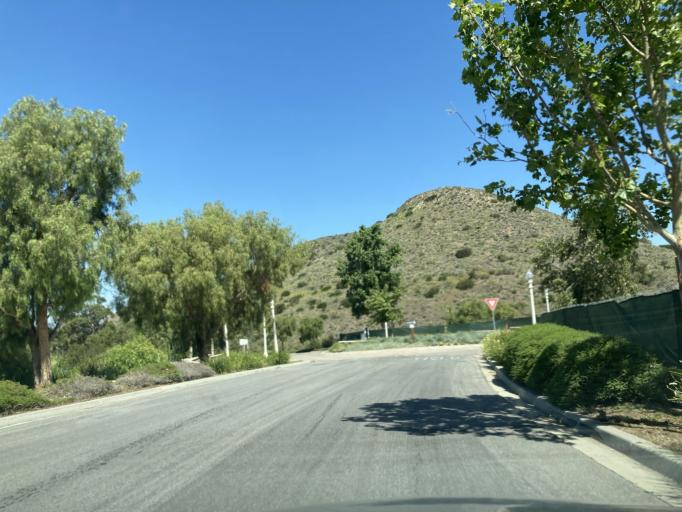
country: US
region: California
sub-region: Ventura County
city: Camarillo
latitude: 34.1706
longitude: -119.0360
